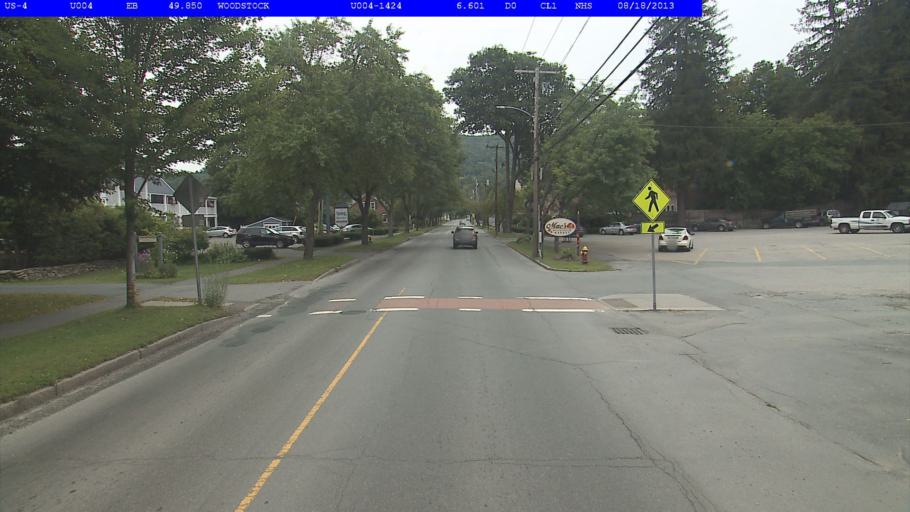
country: US
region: Vermont
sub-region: Windsor County
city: Woodstock
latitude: 43.6268
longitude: -72.5124
